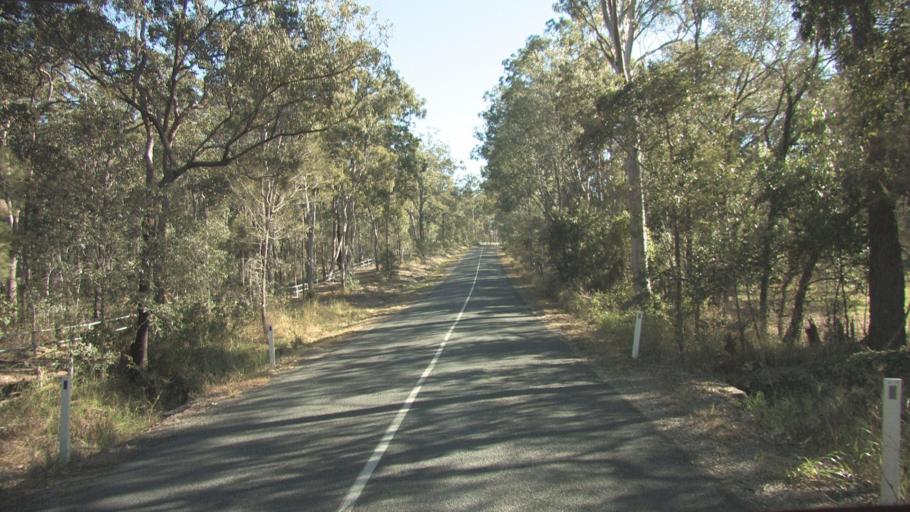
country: AU
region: Queensland
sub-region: Gold Coast
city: Ormeau Hills
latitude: -27.8209
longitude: 153.1698
